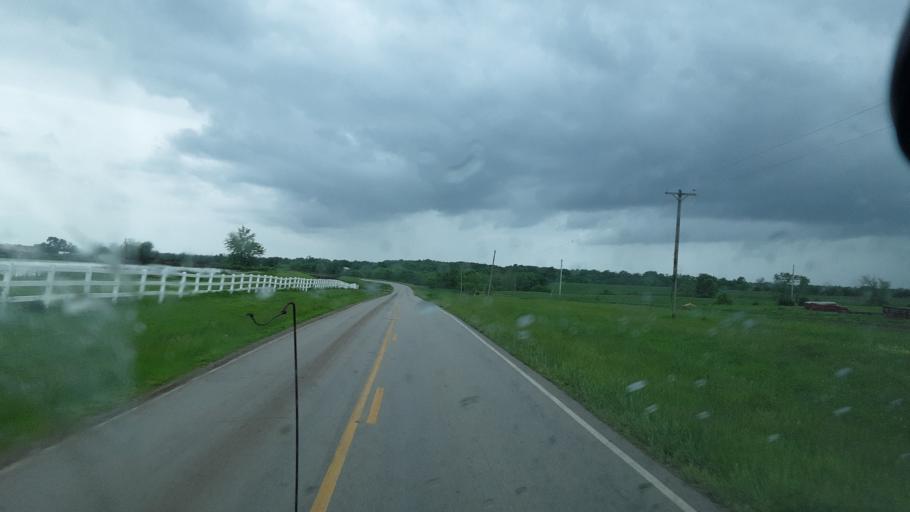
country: US
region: Missouri
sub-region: Monroe County
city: Paris
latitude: 39.4618
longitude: -92.2127
